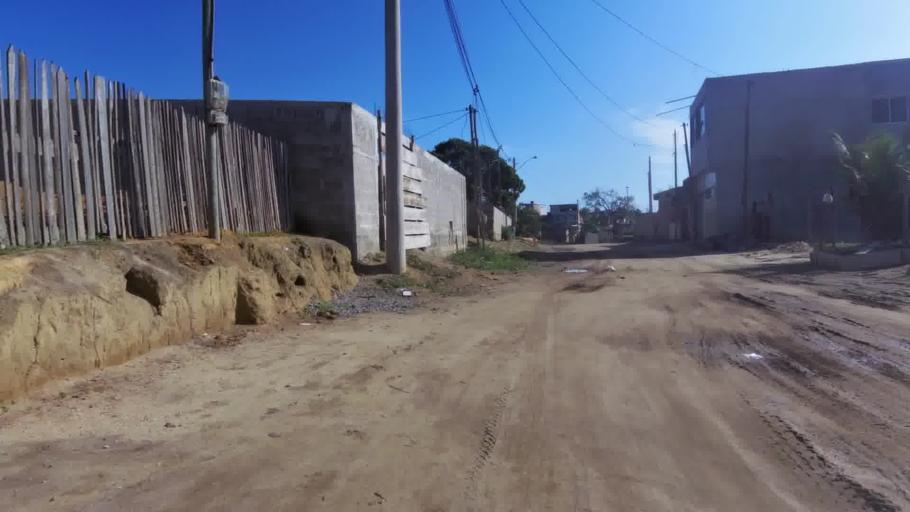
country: BR
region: Espirito Santo
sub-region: Piuma
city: Piuma
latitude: -20.8196
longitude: -40.6195
